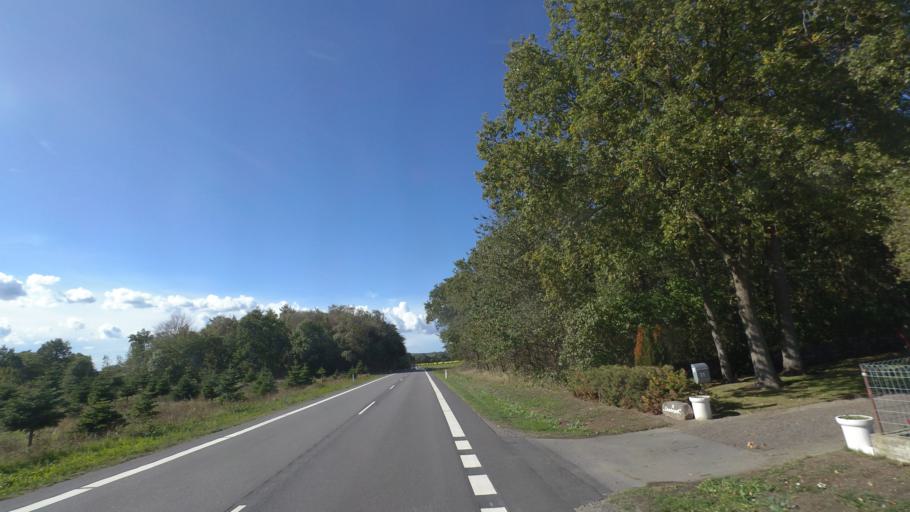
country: DK
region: Capital Region
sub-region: Bornholm Kommune
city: Akirkeby
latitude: 55.0683
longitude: 14.9934
